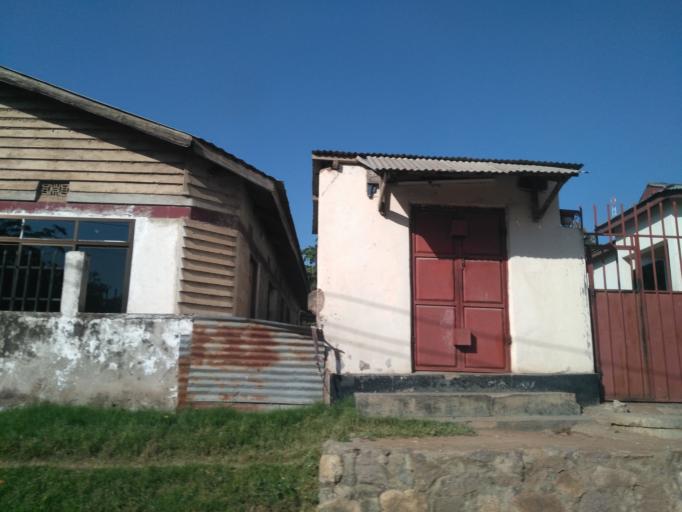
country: TZ
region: Mwanza
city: Mwanza
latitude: -2.5038
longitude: 32.8917
